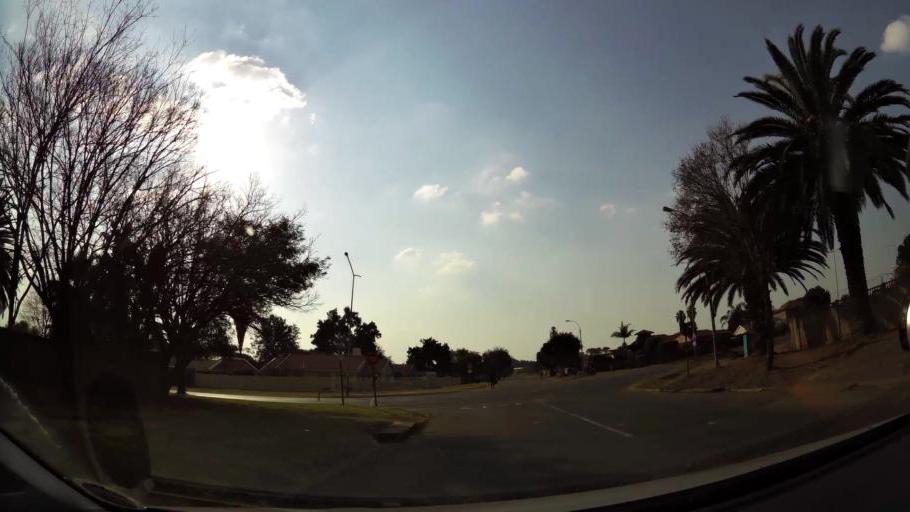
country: ZA
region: Gauteng
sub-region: City of Johannesburg Metropolitan Municipality
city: Modderfontein
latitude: -26.1016
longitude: 28.1927
